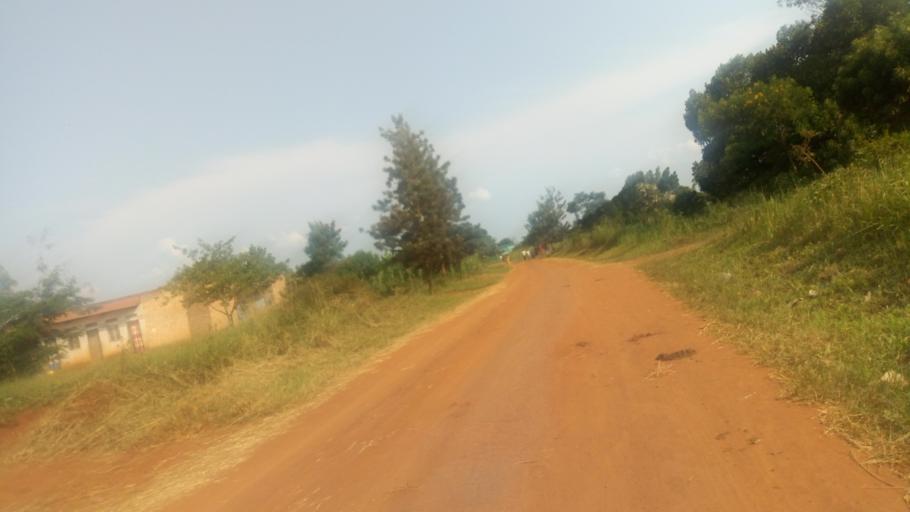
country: UG
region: Western Region
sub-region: Kiryandongo District
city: Kiryandongo
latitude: 1.8076
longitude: 32.0077
